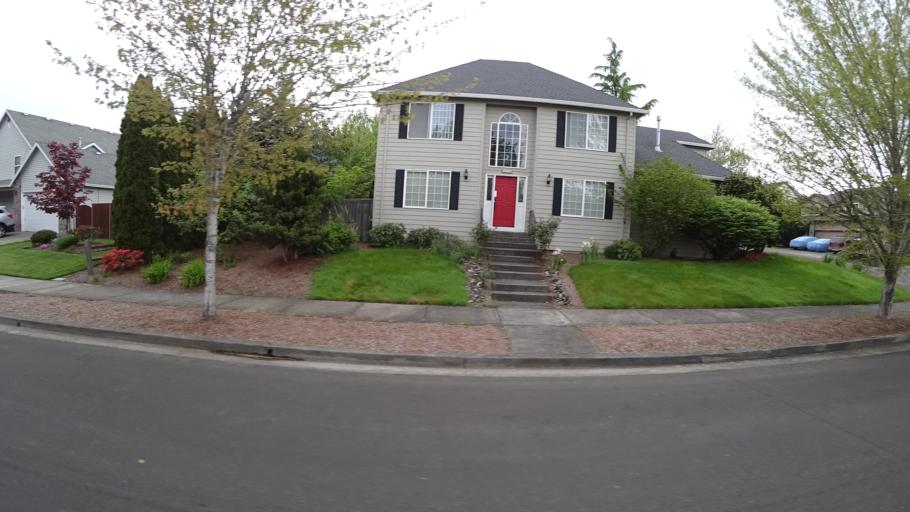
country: US
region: Oregon
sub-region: Washington County
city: Hillsboro
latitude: 45.5472
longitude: -122.9702
